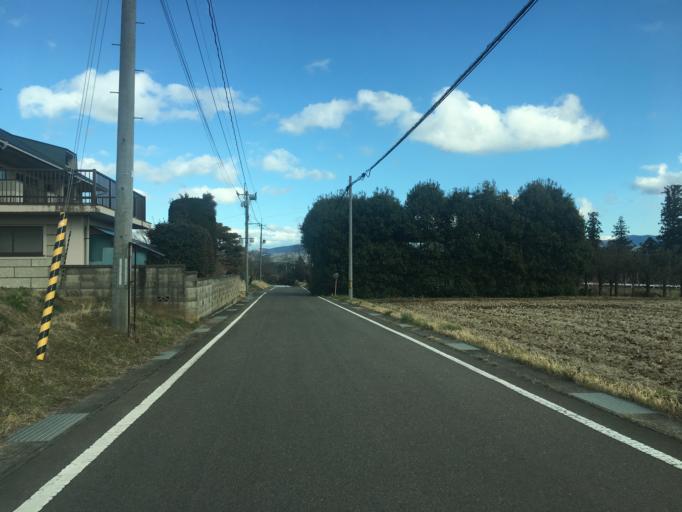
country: JP
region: Fukushima
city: Yanagawamachi-saiwaicho
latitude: 37.8871
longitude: 140.5767
